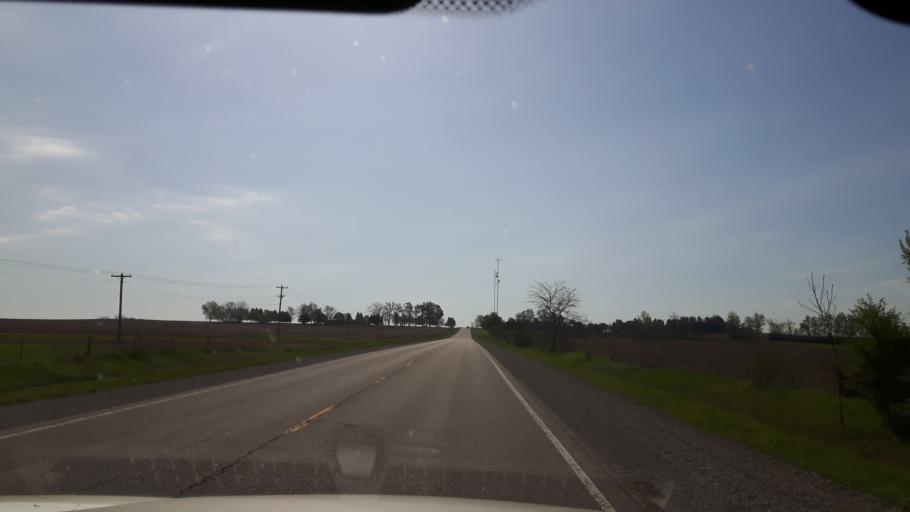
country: CA
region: Ontario
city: Bluewater
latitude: 43.5246
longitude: -81.5601
